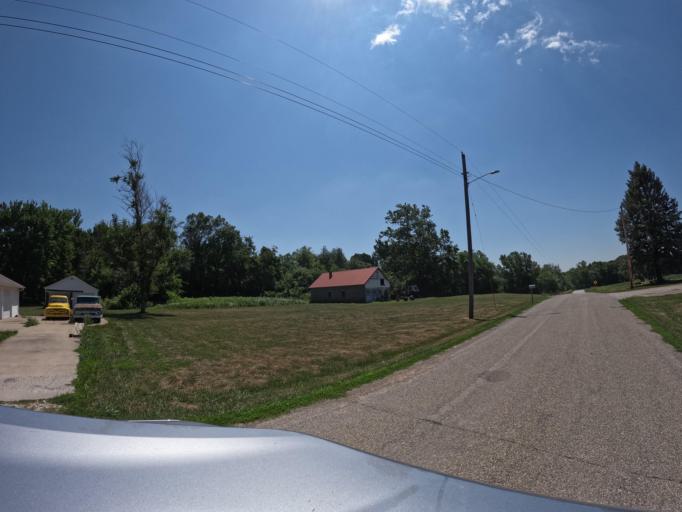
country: US
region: Iowa
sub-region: Keokuk County
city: Sigourney
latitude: 41.2614
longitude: -92.2502
